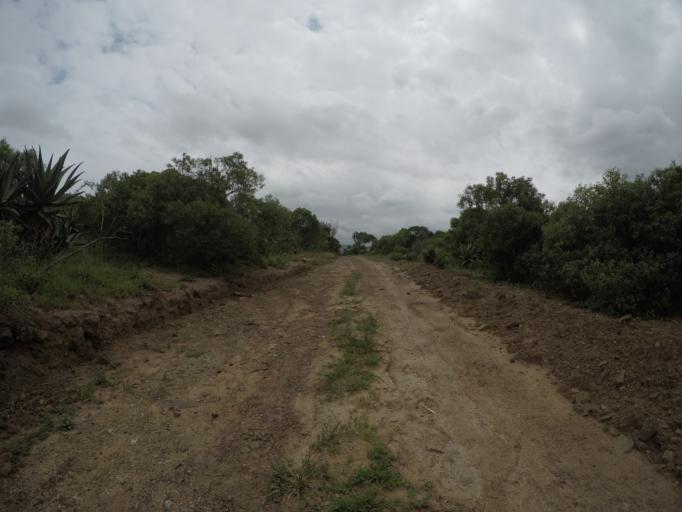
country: ZA
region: KwaZulu-Natal
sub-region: uThungulu District Municipality
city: Empangeni
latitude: -28.6056
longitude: 31.8306
